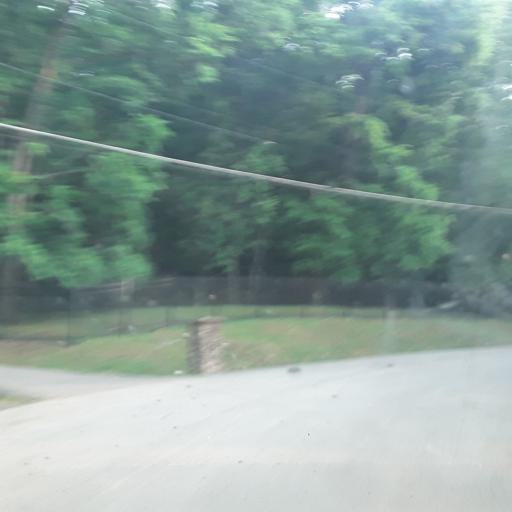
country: US
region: Tennessee
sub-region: Williamson County
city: Brentwood
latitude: 36.0585
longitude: -86.7828
